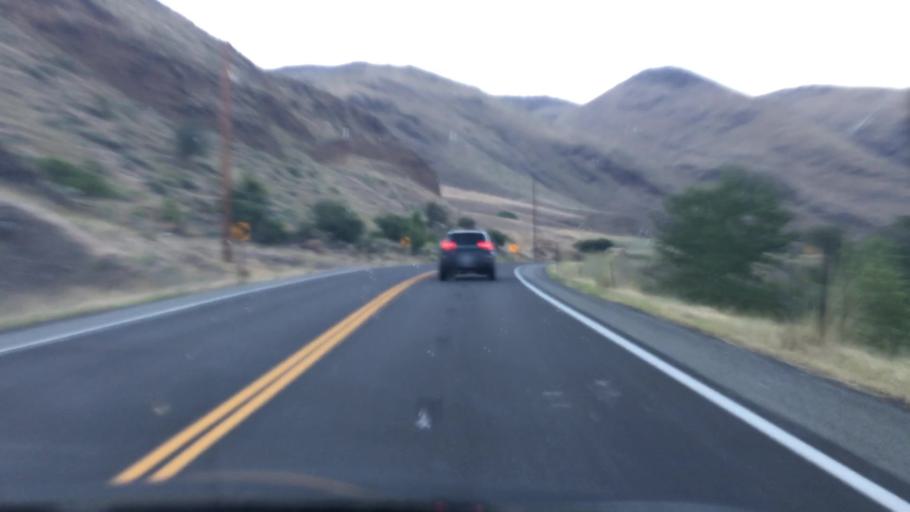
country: US
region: Idaho
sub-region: Valley County
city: McCall
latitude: 45.3891
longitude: -116.3491
